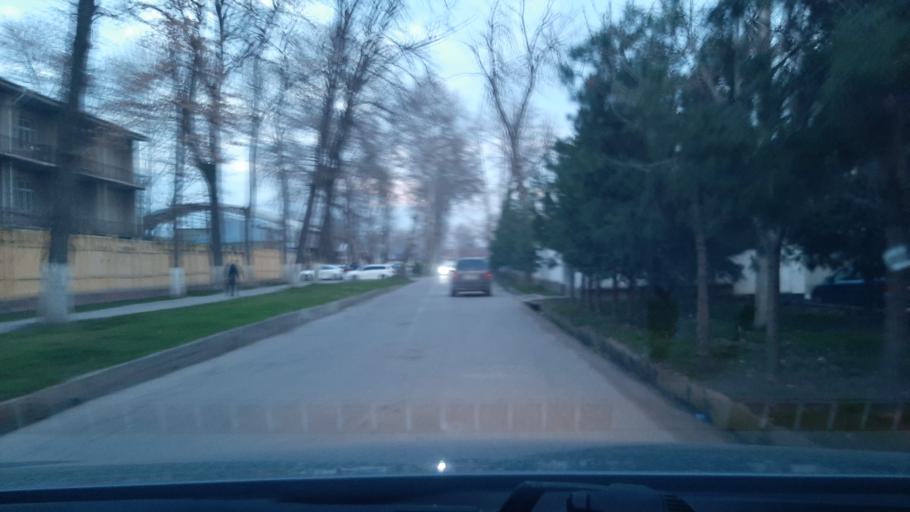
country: TJ
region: Dushanbe
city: Dushanbe
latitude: 38.5705
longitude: 68.7631
